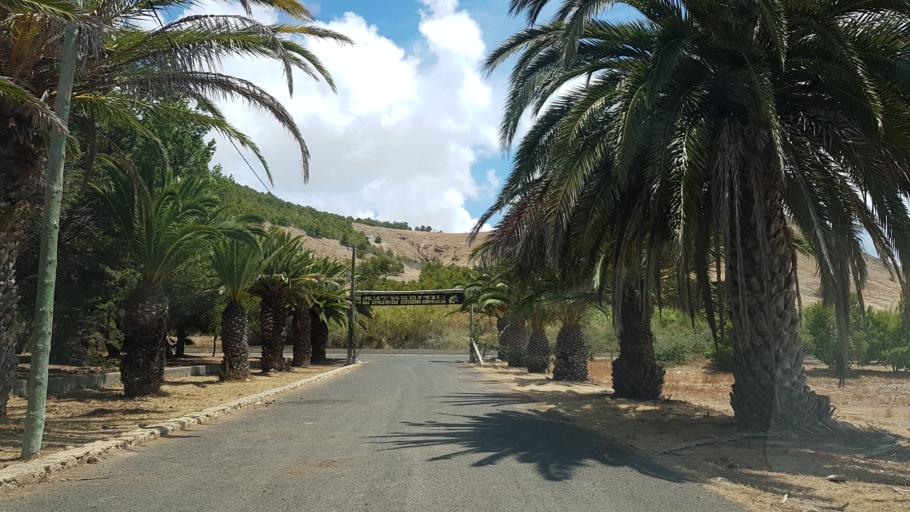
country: PT
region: Madeira
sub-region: Porto Santo
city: Vila de Porto Santo
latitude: 33.0371
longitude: -16.3716
